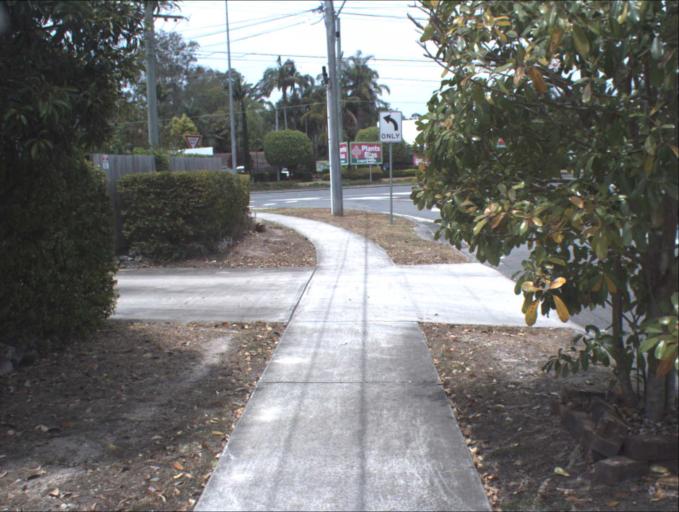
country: AU
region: Queensland
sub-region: Logan
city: Beenleigh
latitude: -27.6708
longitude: 153.1903
